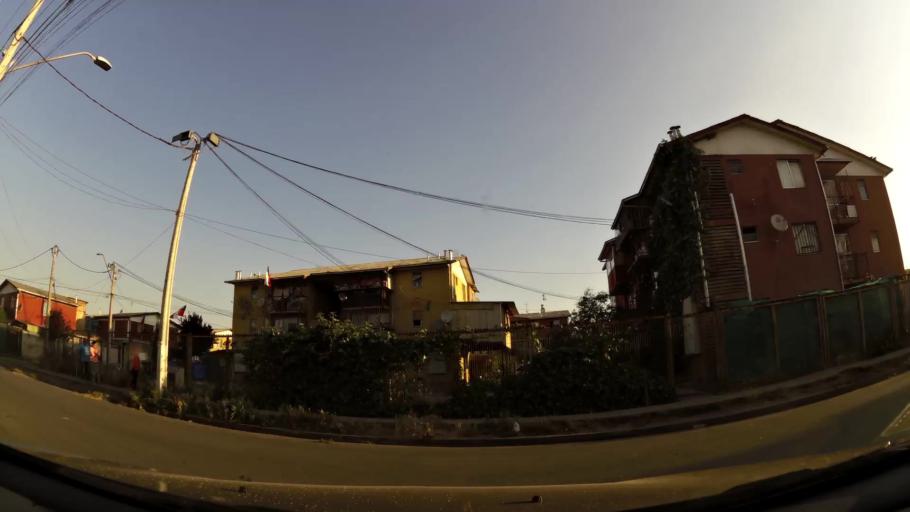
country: CL
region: Santiago Metropolitan
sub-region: Provincia de Maipo
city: San Bernardo
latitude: -33.5970
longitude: -70.6728
